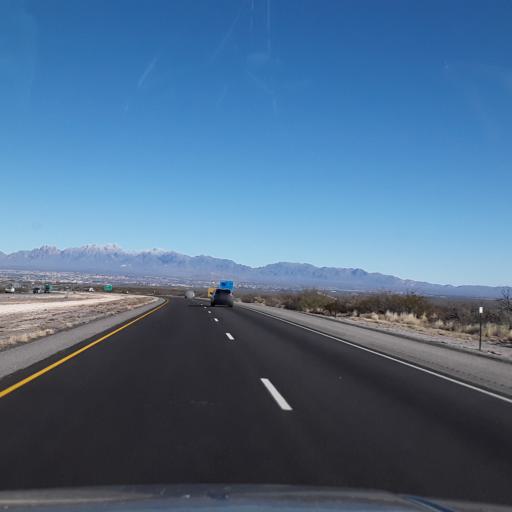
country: US
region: New Mexico
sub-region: Dona Ana County
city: Mesilla
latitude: 32.2732
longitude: -106.9114
